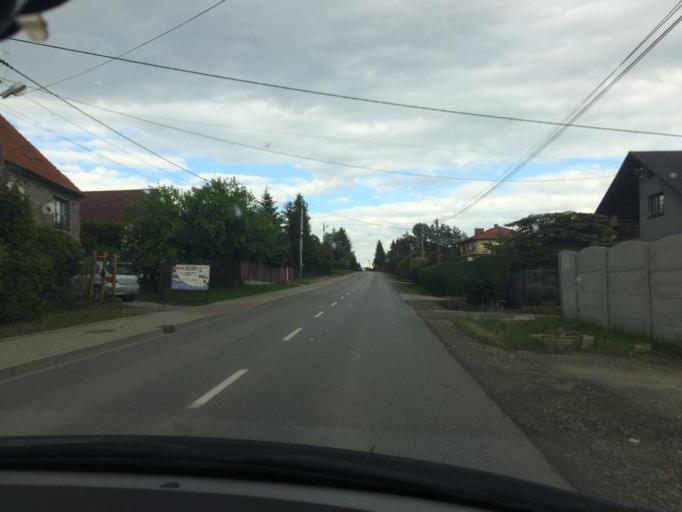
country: PL
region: Lesser Poland Voivodeship
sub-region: Powiat krakowski
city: Ochojno
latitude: 49.9745
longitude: 20.0062
